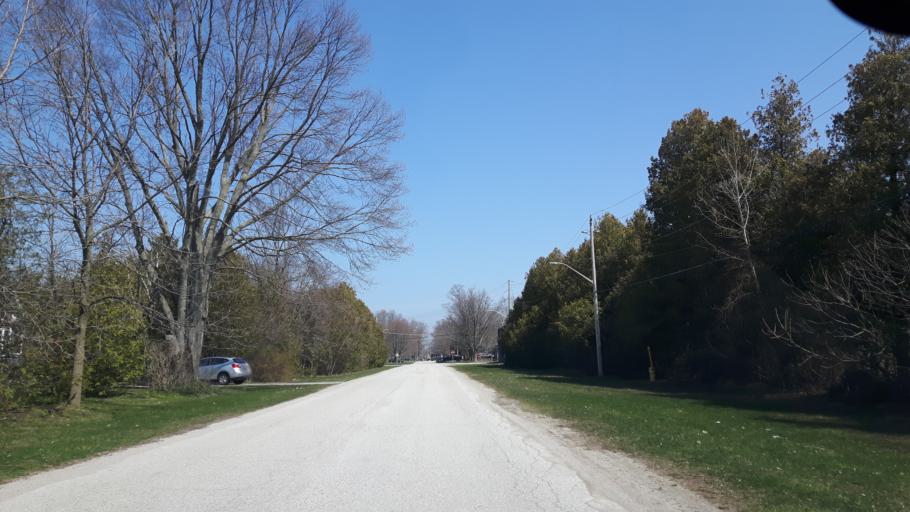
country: CA
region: Ontario
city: Bluewater
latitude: 43.5590
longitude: -81.6980
